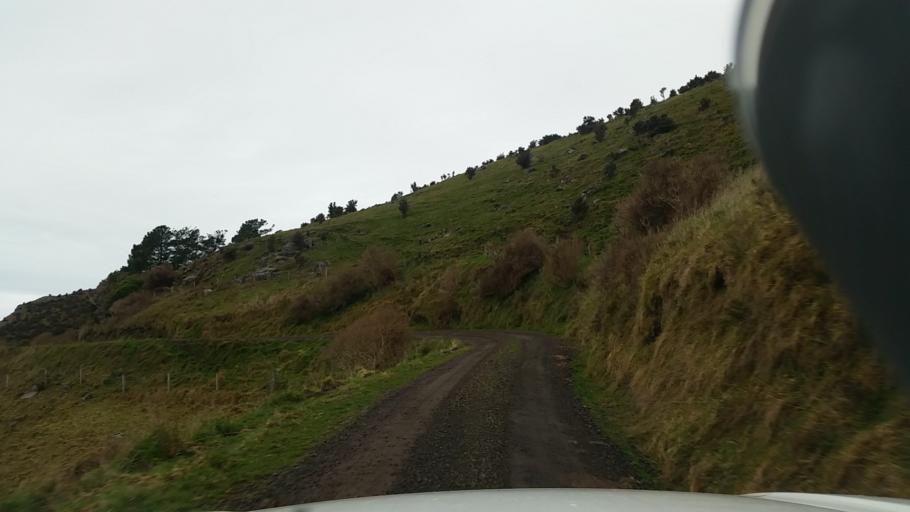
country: NZ
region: Canterbury
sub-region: Christchurch City
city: Christchurch
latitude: -43.7450
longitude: 173.0108
